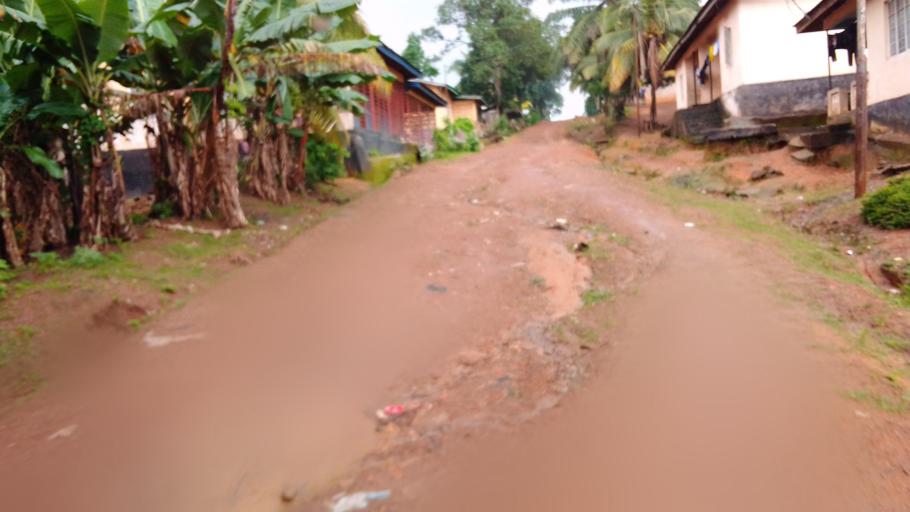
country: SL
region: Eastern Province
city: Kenema
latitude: 7.8795
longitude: -11.1775
